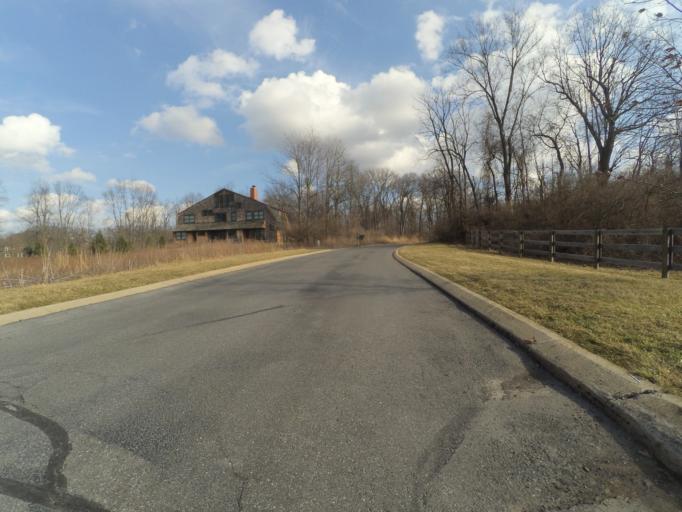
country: US
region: Pennsylvania
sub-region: Centre County
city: Park Forest Village
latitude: 40.8103
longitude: -77.9572
